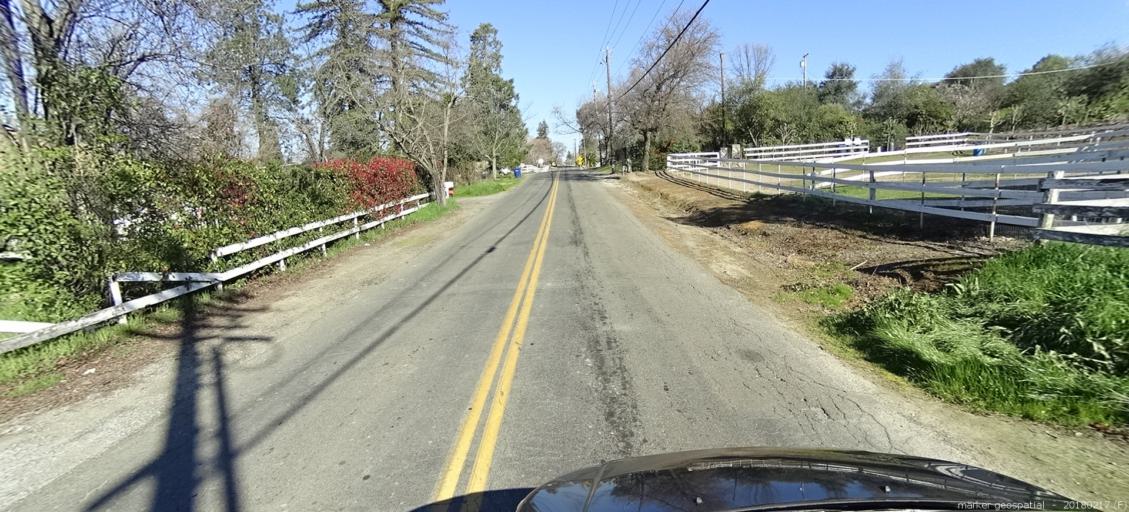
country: US
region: California
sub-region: Sacramento County
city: Orangevale
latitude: 38.7008
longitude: -121.2018
